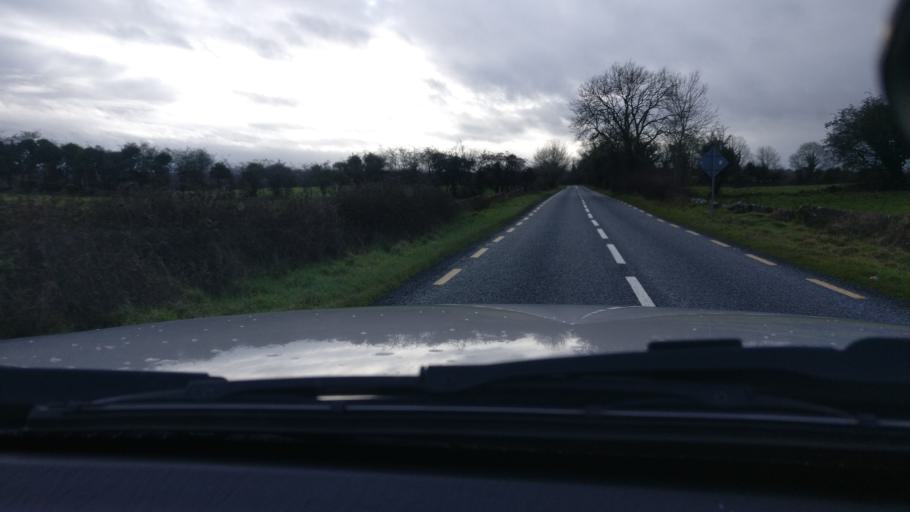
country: IE
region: Leinster
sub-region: An Iarmhi
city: Moate
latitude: 53.6150
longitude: -7.7050
